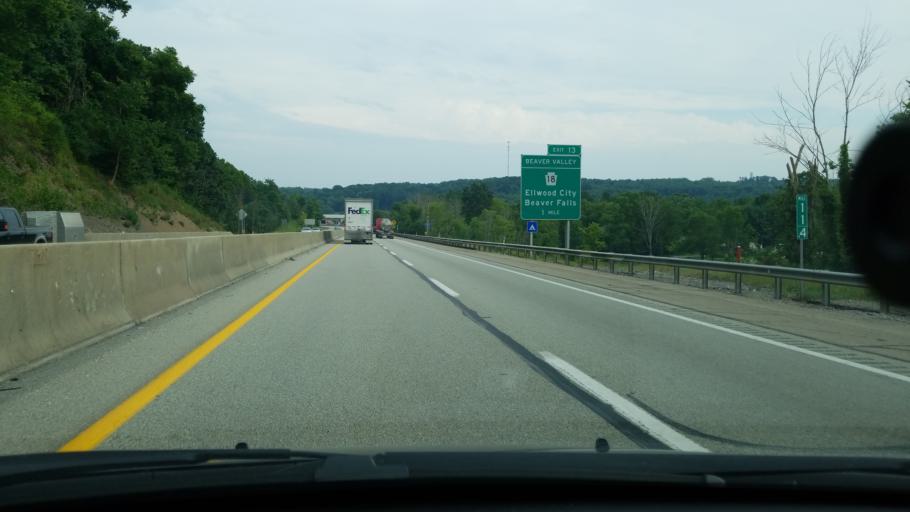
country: US
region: Pennsylvania
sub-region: Beaver County
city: Big Beaver
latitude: 40.8249
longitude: -80.3475
